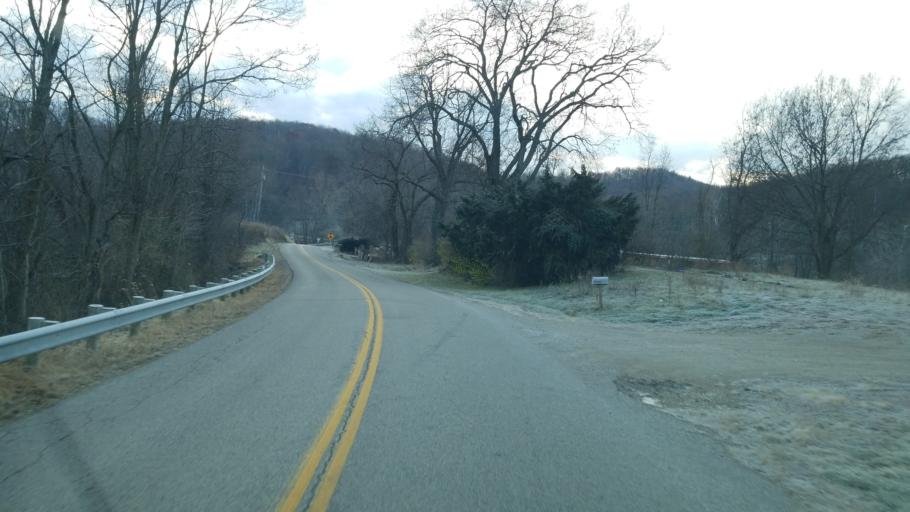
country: US
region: Ohio
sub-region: Ross County
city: Chillicothe
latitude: 39.2356
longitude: -82.8973
